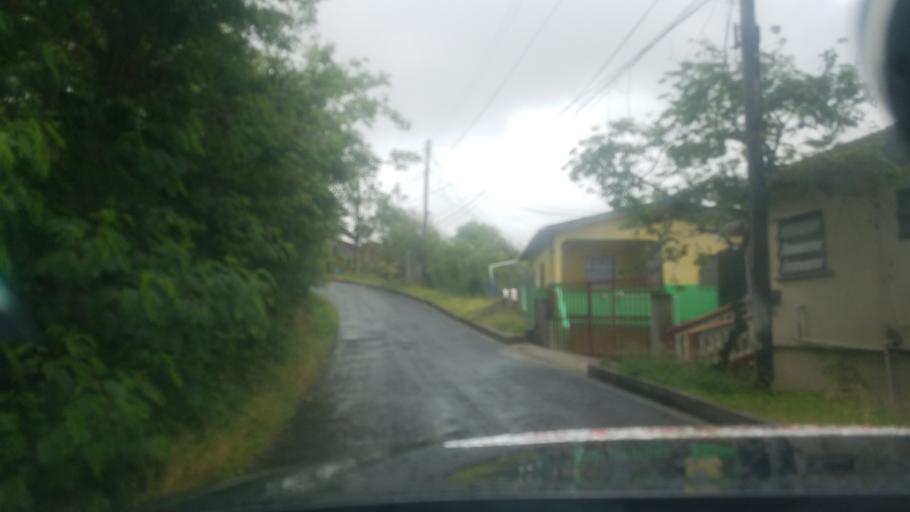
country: LC
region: Laborie Quarter
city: Laborie
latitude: 13.7490
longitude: -60.9683
